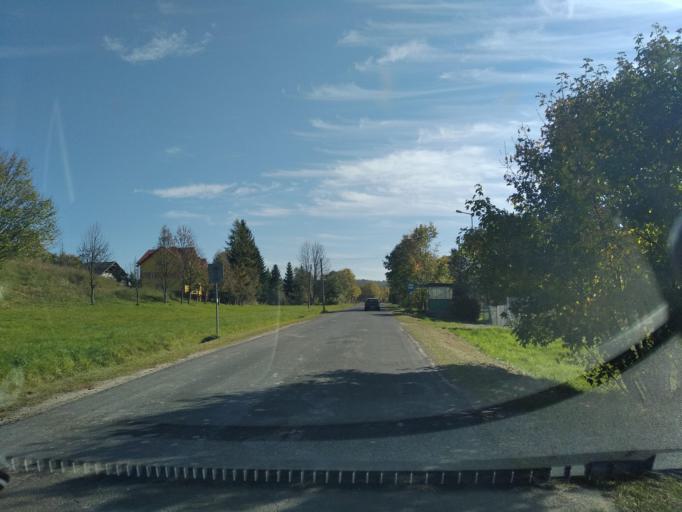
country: PL
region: Subcarpathian Voivodeship
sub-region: Powiat sanocki
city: Komancza
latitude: 49.3912
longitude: 21.9859
